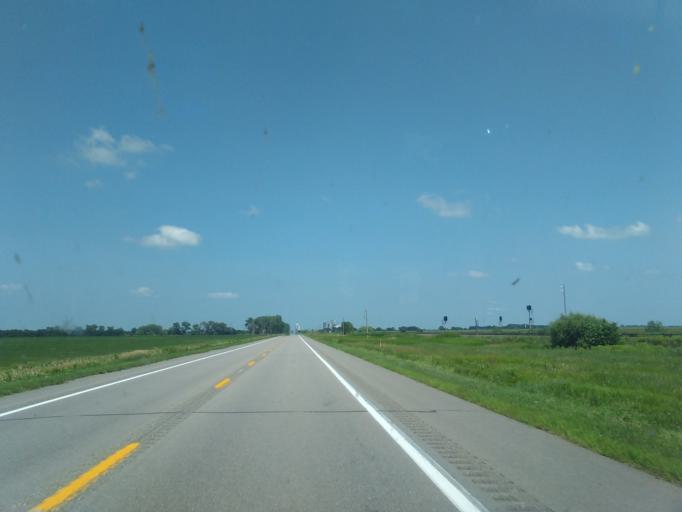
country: US
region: Nebraska
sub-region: Phelps County
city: Holdrege
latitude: 40.7236
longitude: -99.4220
